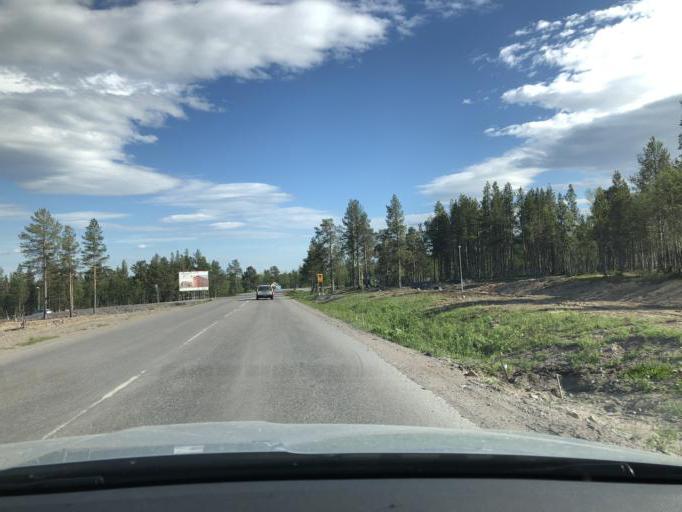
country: SE
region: Norrbotten
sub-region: Kiruna Kommun
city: Kiruna
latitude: 67.8525
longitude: 20.2762
